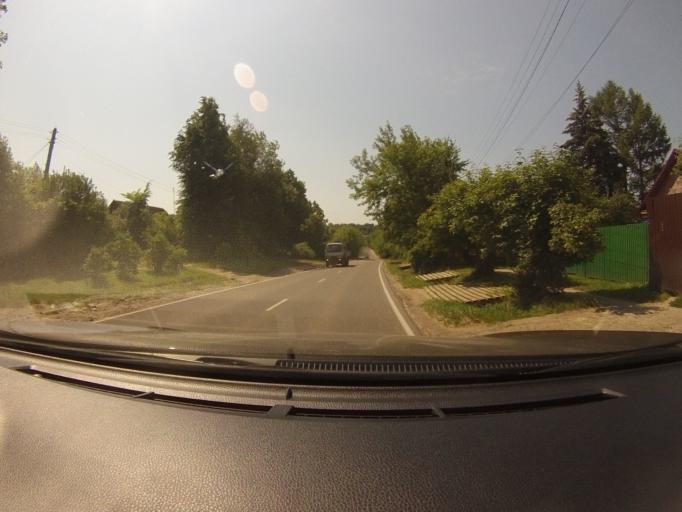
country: RU
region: Kaluga
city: Maloyaroslavets
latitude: 54.9998
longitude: 36.4708
